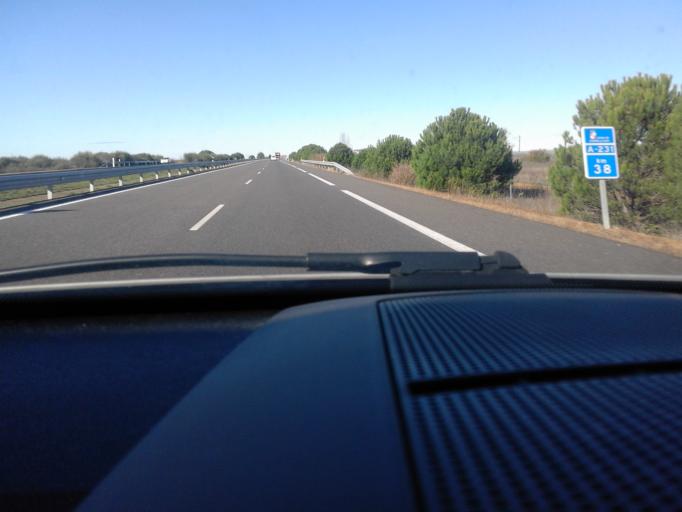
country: ES
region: Castille and Leon
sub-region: Provincia de Leon
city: Bercianos del Real Camino
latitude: 42.4041
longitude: -5.1746
